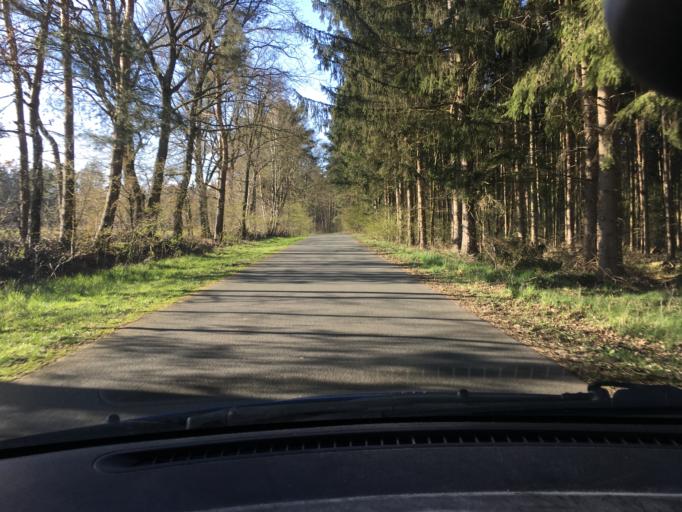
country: DE
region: Lower Saxony
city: Bispingen
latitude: 53.1075
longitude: 10.0470
